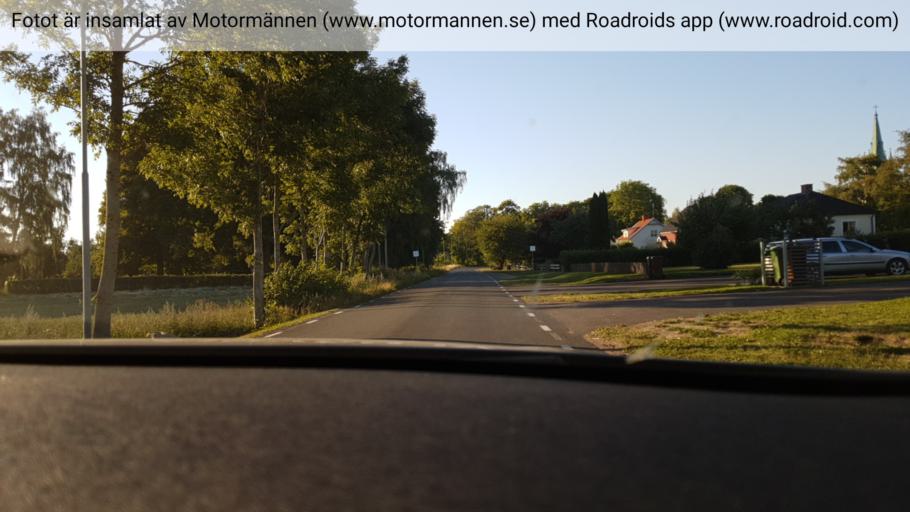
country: SE
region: Vaestra Goetaland
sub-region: Skovde Kommun
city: Skultorp
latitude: 58.2497
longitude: 13.7847
